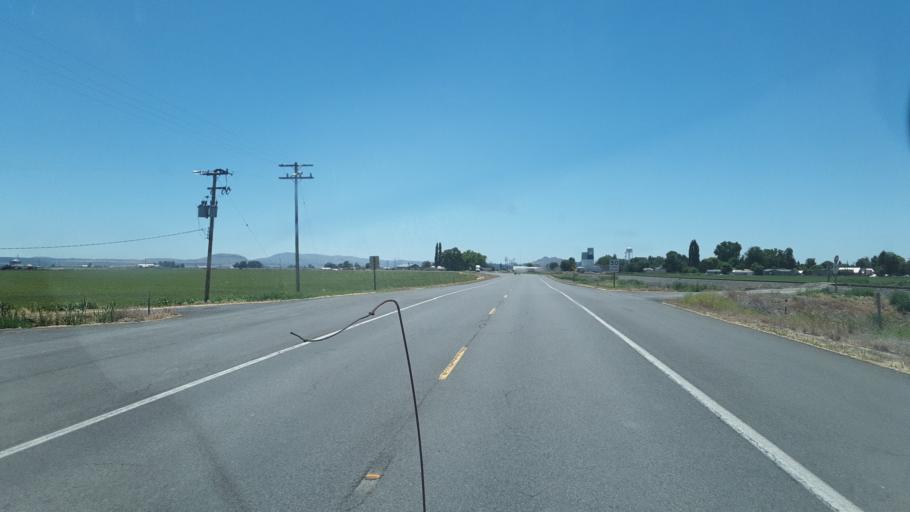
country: US
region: California
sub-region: Siskiyou County
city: Tulelake
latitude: 41.9644
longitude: -121.4820
